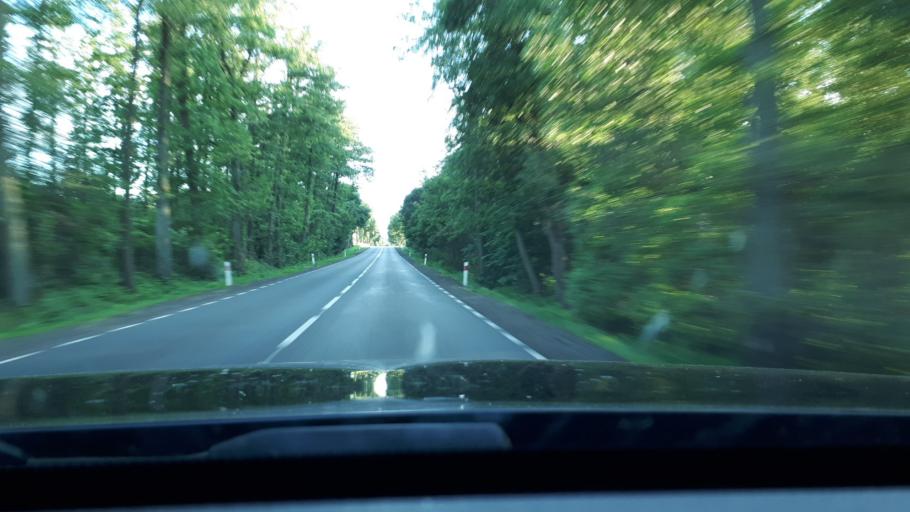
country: PL
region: Masovian Voivodeship
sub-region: Powiat ciechanowski
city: Ojrzen
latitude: 52.8053
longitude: 20.6003
